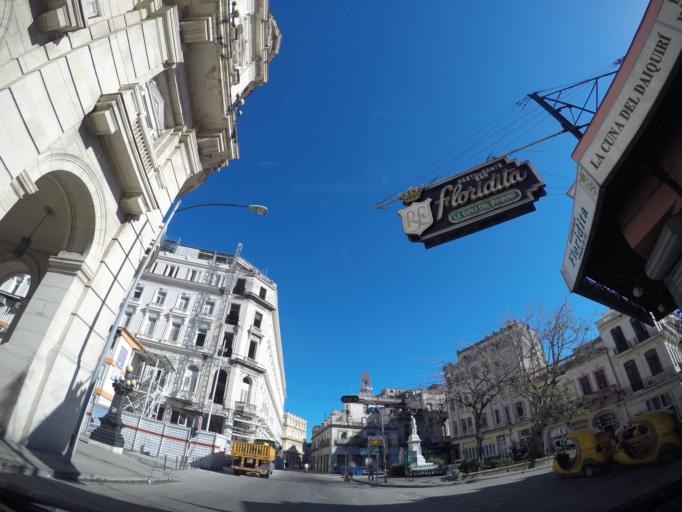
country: CU
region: La Habana
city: Centro Habana
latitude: 23.1374
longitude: -82.3575
